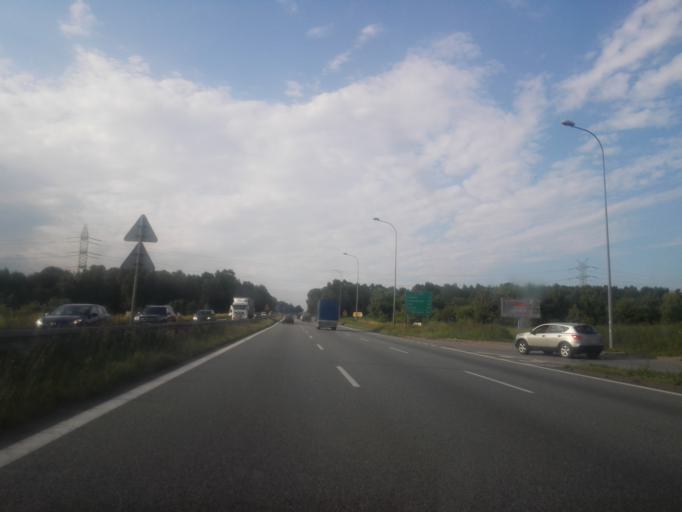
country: PL
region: Silesian Voivodeship
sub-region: Powiat bedzinski
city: Siewierz
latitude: 50.4294
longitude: 19.2148
